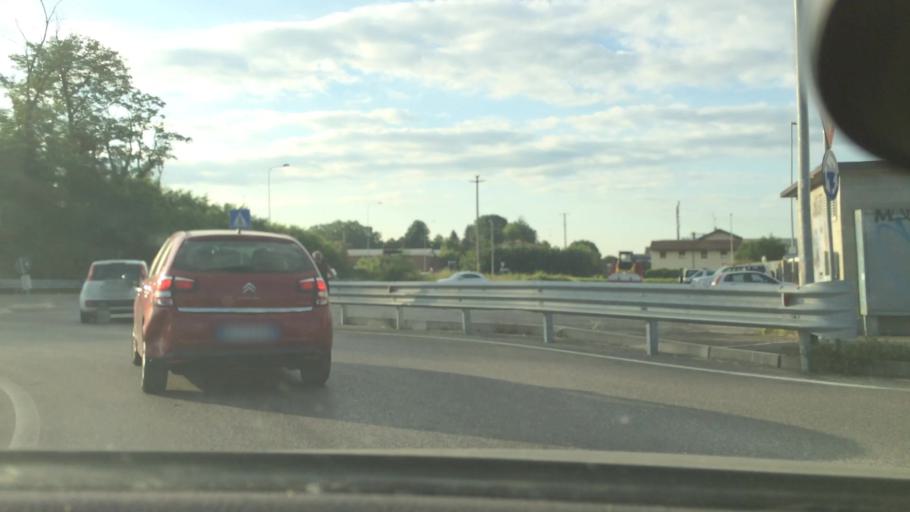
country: IT
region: Lombardy
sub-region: Citta metropolitana di Milano
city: Pregnana Milanese
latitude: 45.5268
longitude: 9.0095
